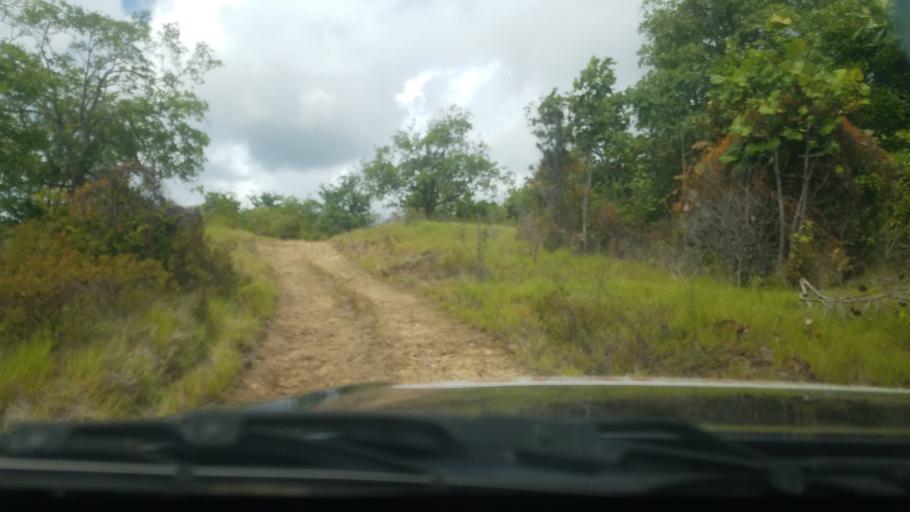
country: LC
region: Praslin
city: Praslin
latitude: 13.8682
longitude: -60.8896
